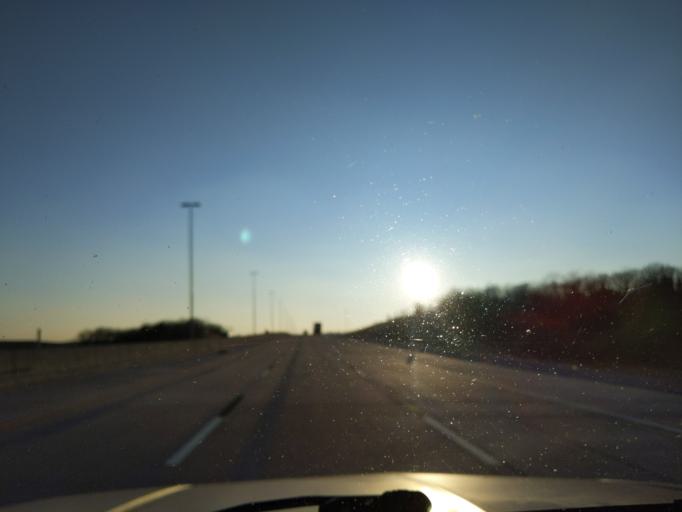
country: US
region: Oklahoma
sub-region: Creek County
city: Kellyville
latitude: 35.9521
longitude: -96.2428
